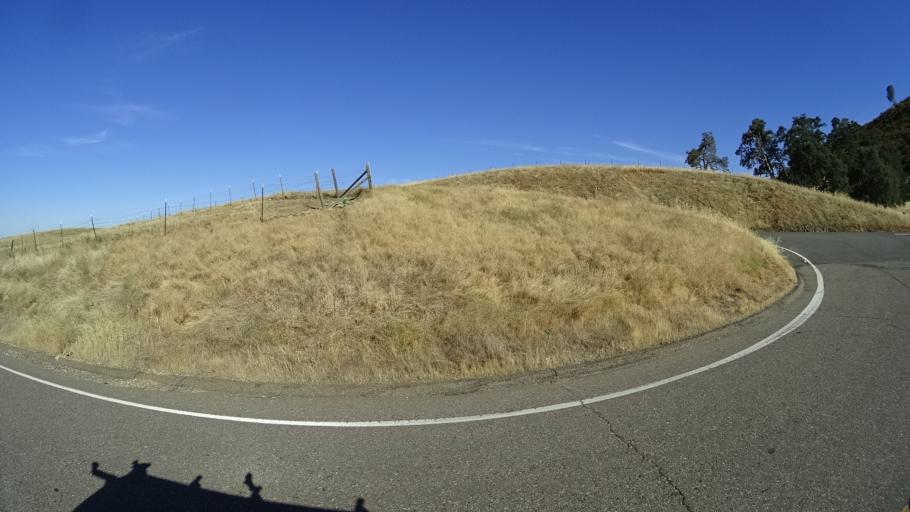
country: US
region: California
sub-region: Calaveras County
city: Valley Springs
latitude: 38.1971
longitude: -120.8007
